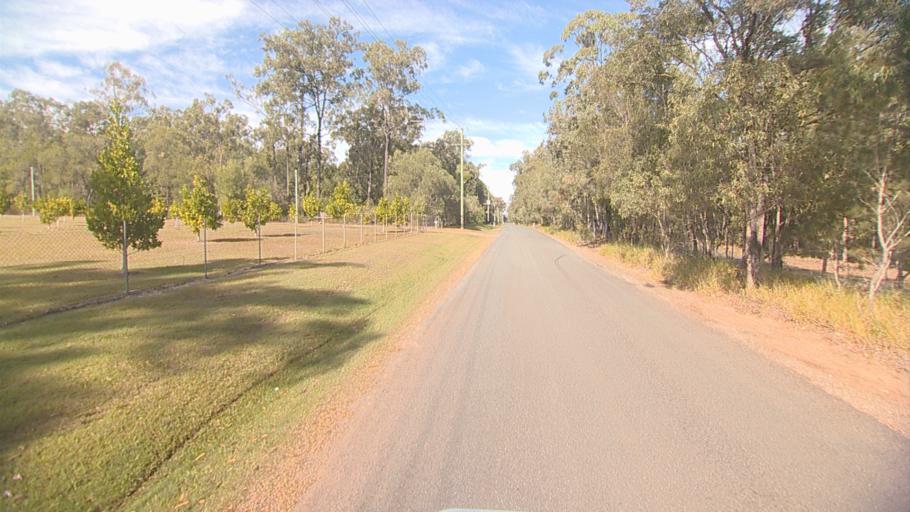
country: AU
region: Queensland
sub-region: Brisbane
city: Forest Lake
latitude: -27.6525
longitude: 152.9834
